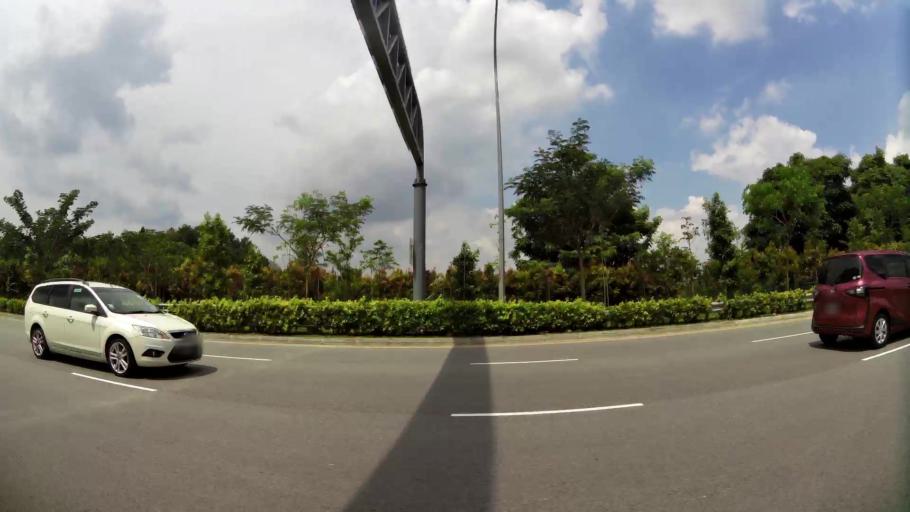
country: MY
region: Johor
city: Kampung Pasir Gudang Baru
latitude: 1.4051
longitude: 103.8551
